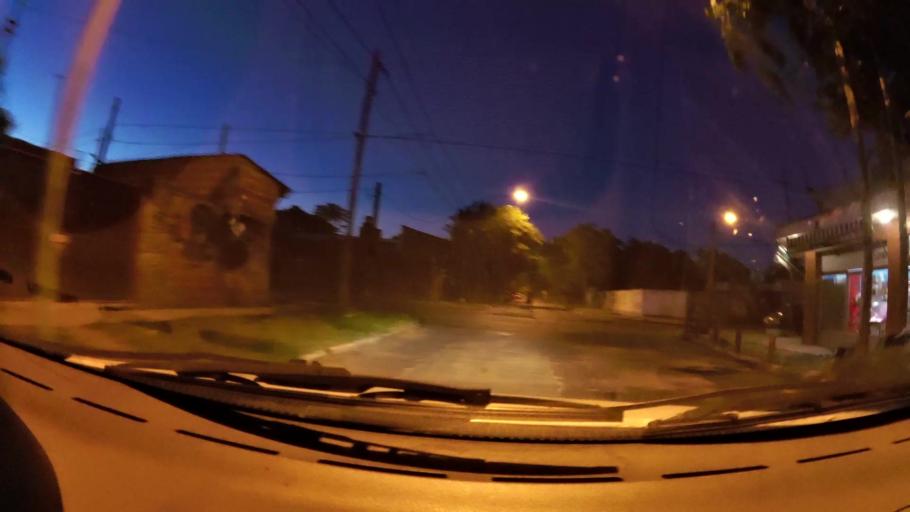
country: AR
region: Buenos Aires
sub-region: Partido de Quilmes
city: Quilmes
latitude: -34.7691
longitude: -58.1896
